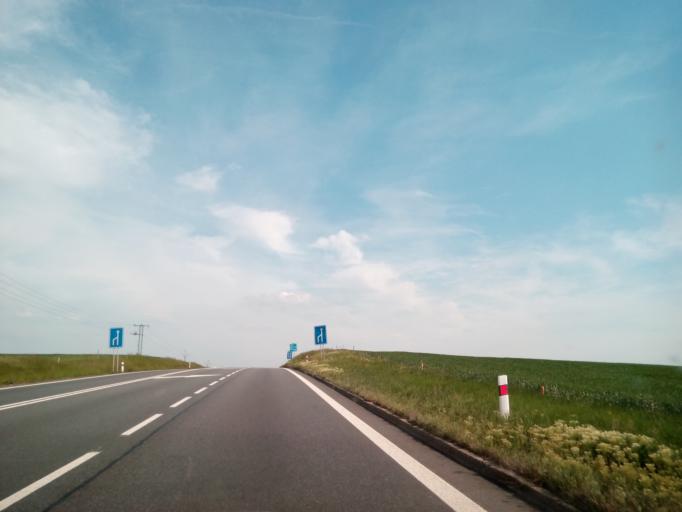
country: CZ
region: South Moravian
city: Krenovice
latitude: 49.1690
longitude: 16.8392
